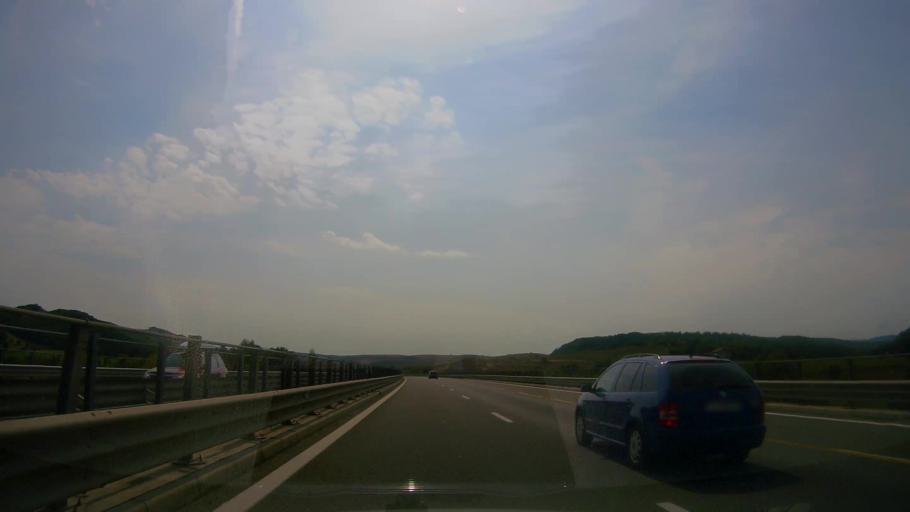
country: RO
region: Cluj
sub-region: Comuna Floresti
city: Luna de Sus
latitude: 46.7162
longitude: 23.4210
